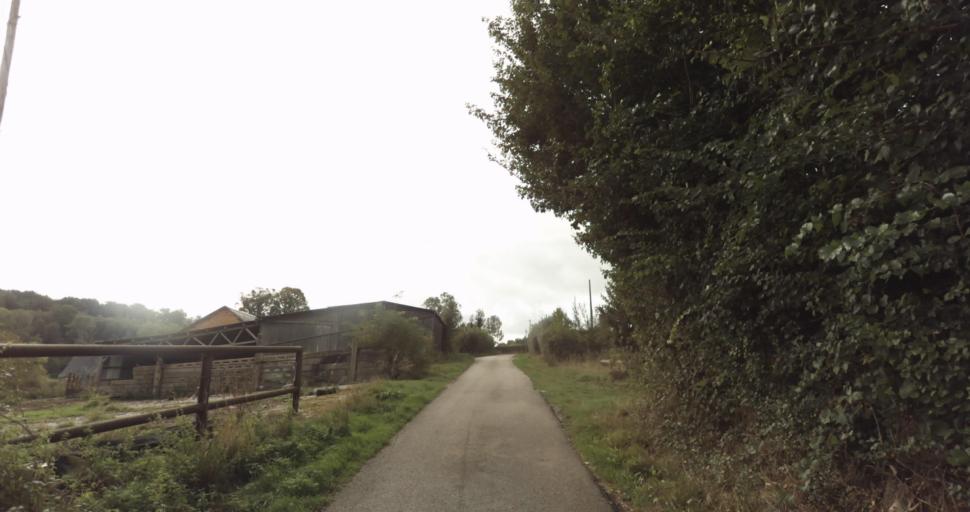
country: FR
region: Lower Normandy
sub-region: Departement de l'Orne
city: Gace
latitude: 48.7961
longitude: 0.2646
